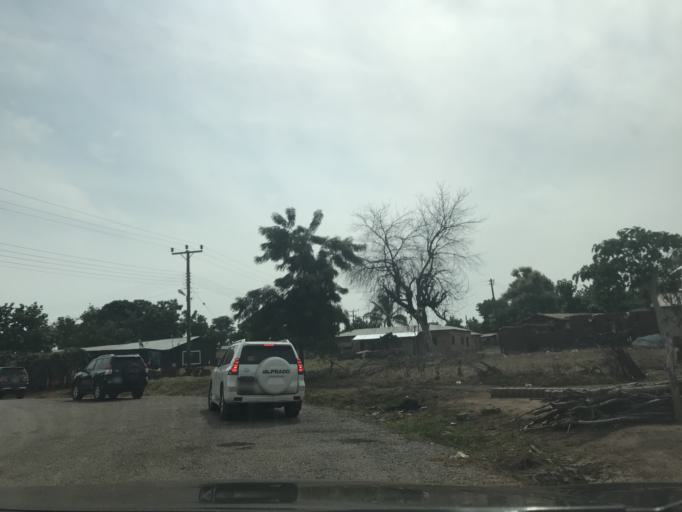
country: GH
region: Upper West
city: Wa
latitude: 10.2602
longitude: -2.5577
